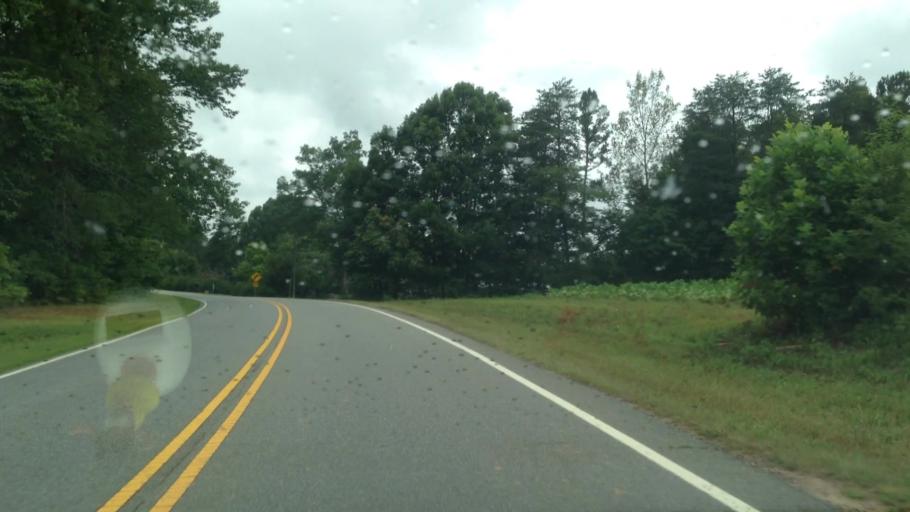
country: US
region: North Carolina
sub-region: Rockingham County
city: Mayodan
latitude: 36.4054
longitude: -80.0445
